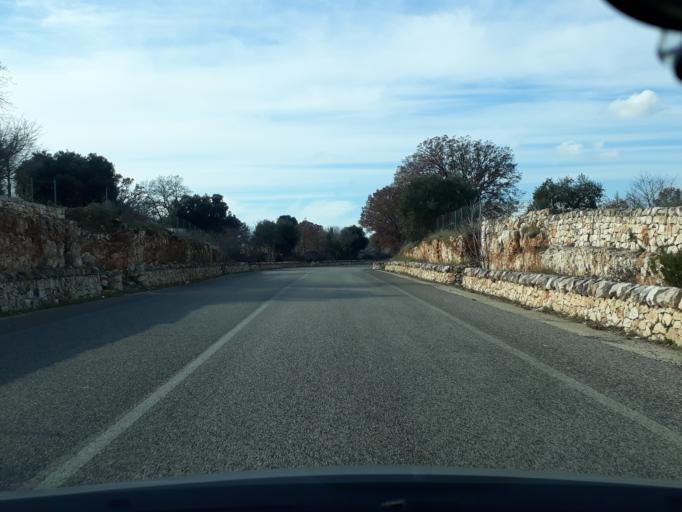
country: IT
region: Apulia
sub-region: Provincia di Bari
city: Locorotondo
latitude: 40.7606
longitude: 17.3362
